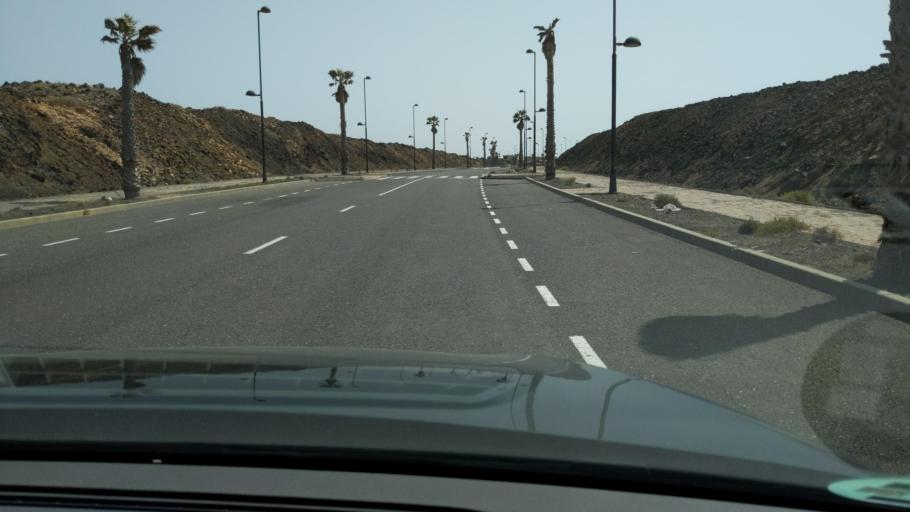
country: ES
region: Canary Islands
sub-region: Provincia de Las Palmas
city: Corralejo
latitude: 28.7364
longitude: -13.9448
